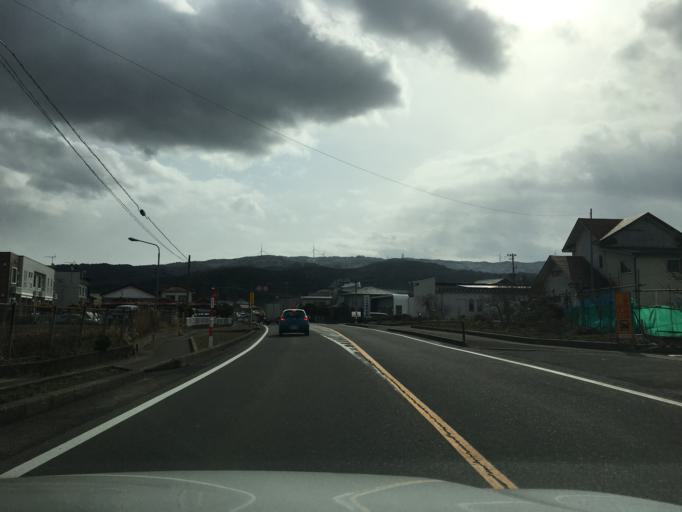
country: JP
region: Yamagata
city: Yuza
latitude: 39.2858
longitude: 139.9581
